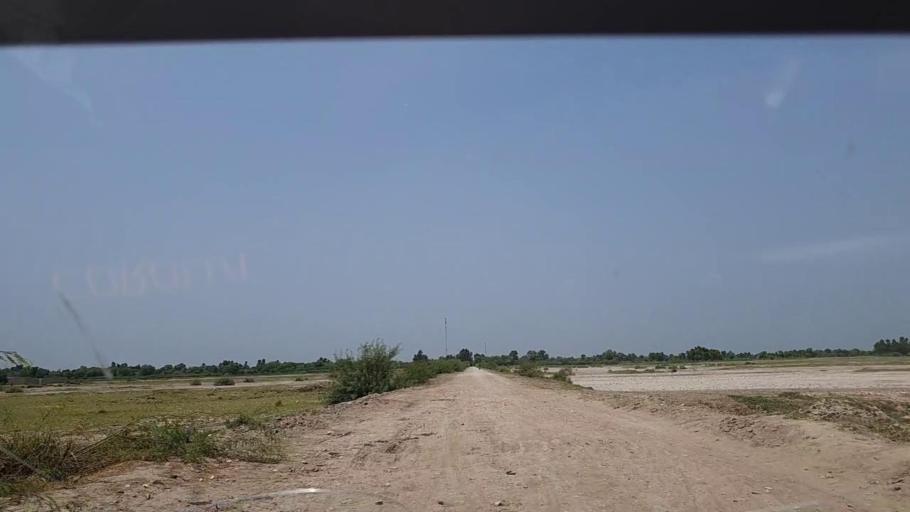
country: PK
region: Sindh
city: Adilpur
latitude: 27.9134
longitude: 69.2114
